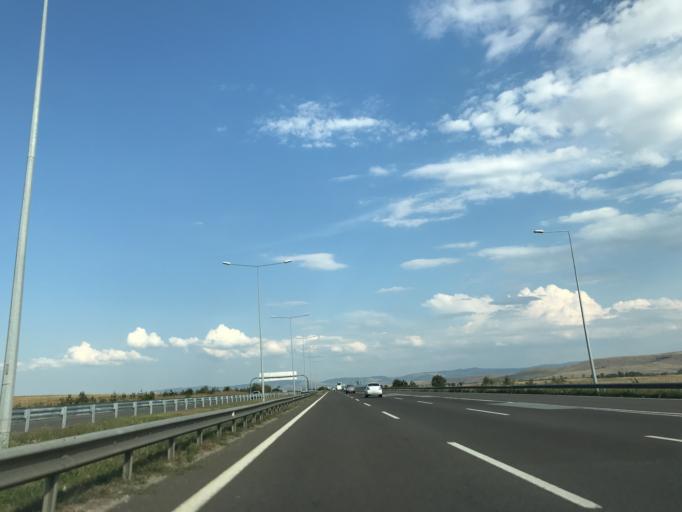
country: TR
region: Bolu
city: Dortdivan
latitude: 40.7421
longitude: 32.1247
